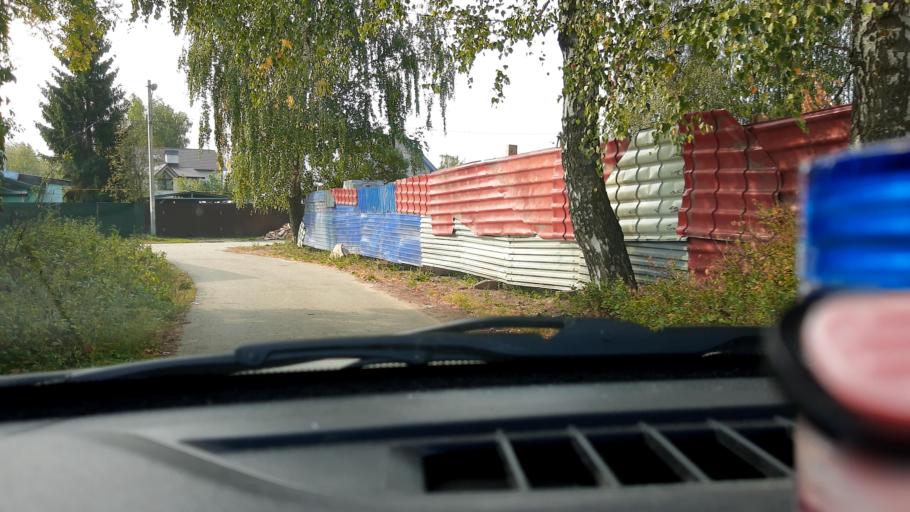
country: RU
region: Nizjnij Novgorod
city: Gorbatovka
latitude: 56.3336
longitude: 43.8201
